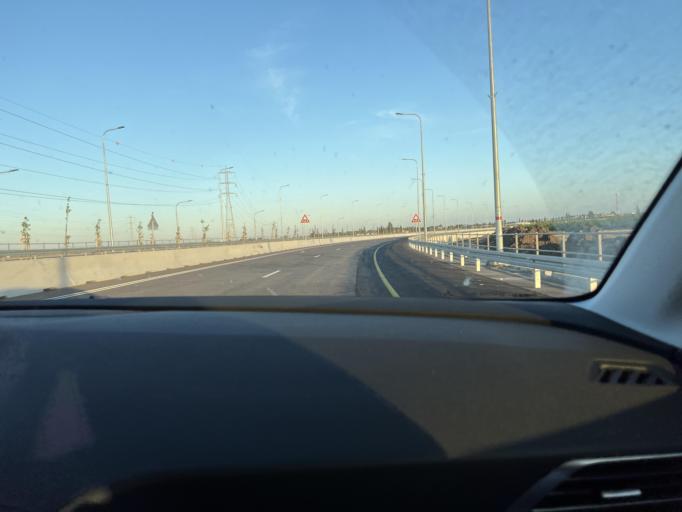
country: IL
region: Central District
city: Gan Yavne
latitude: 31.8101
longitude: 34.7086
